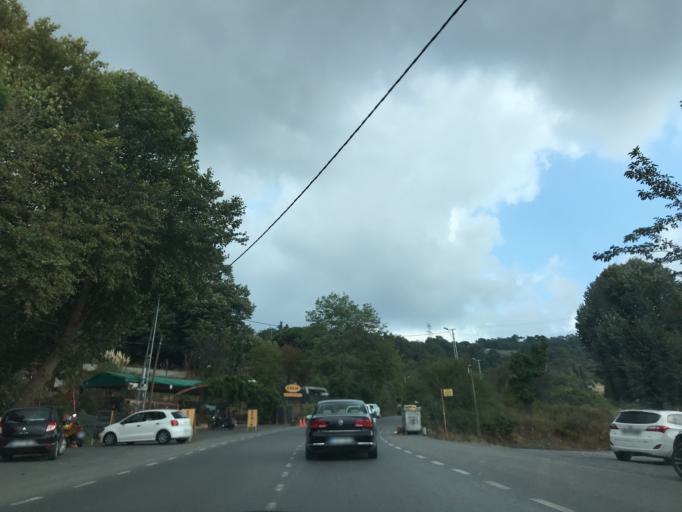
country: TR
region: Istanbul
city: Arikoey
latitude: 41.1805
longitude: 29.0465
